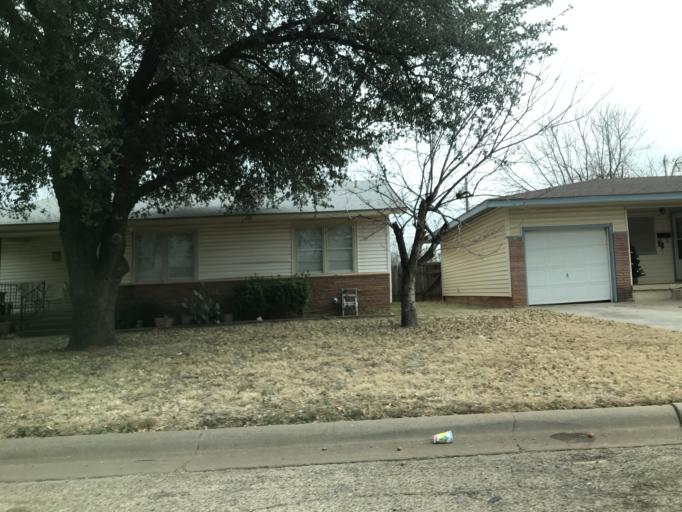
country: US
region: Texas
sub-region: Taylor County
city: Abilene
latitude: 32.4701
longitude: -99.7589
